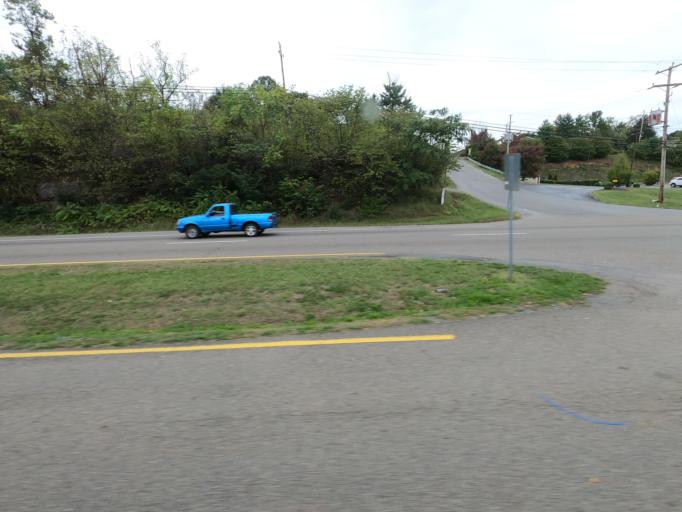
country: US
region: Tennessee
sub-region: Sullivan County
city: Kingsport
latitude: 36.5555
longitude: -82.5940
